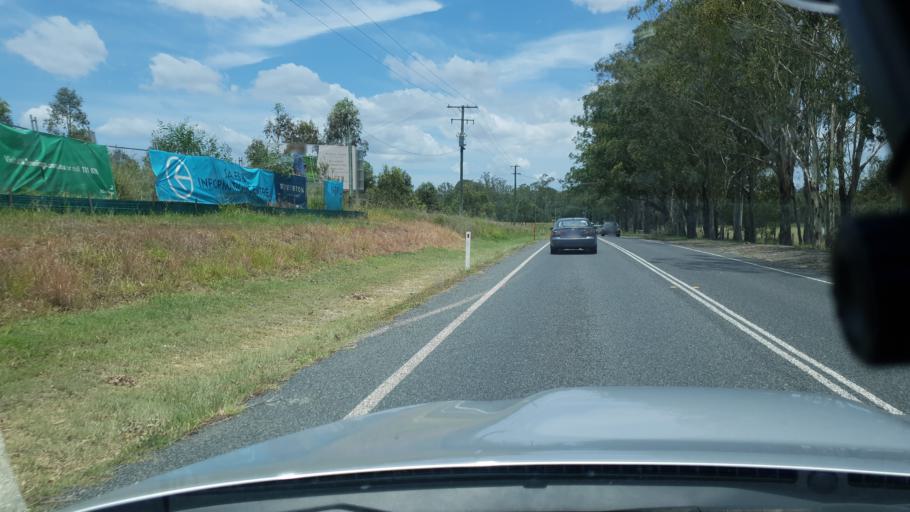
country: AU
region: Queensland
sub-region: Logan
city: North Maclean
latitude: -27.8260
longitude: 153.0119
